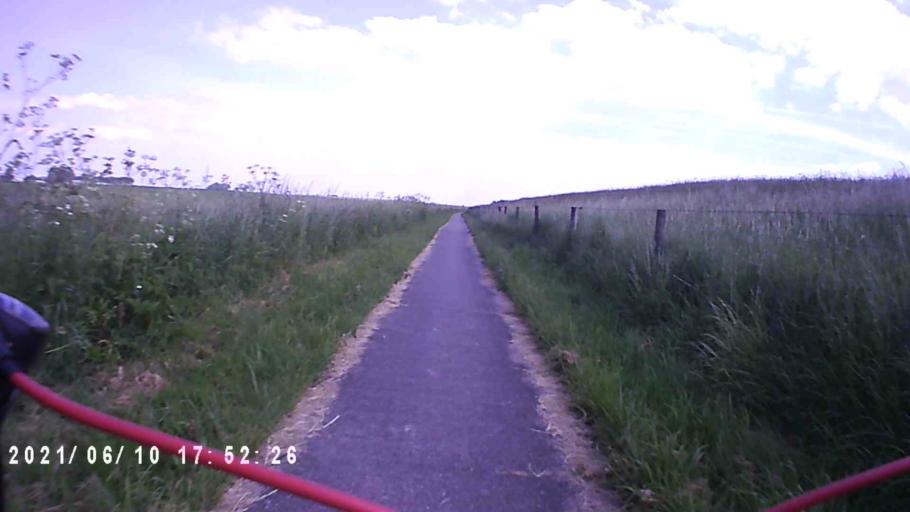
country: NL
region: Groningen
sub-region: Gemeente De Marne
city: Ulrum
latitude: 53.3284
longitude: 6.3181
